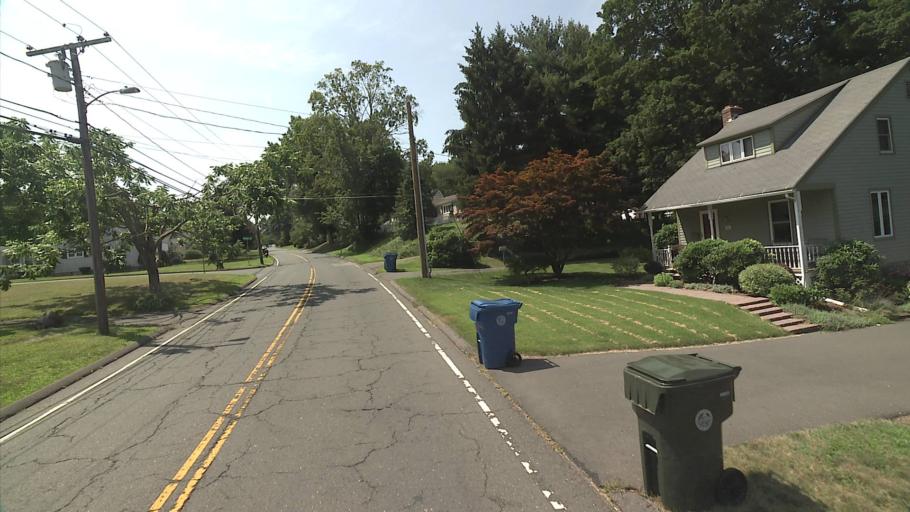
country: US
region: Connecticut
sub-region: Hartford County
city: Kensington
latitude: 41.6252
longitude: -72.7824
